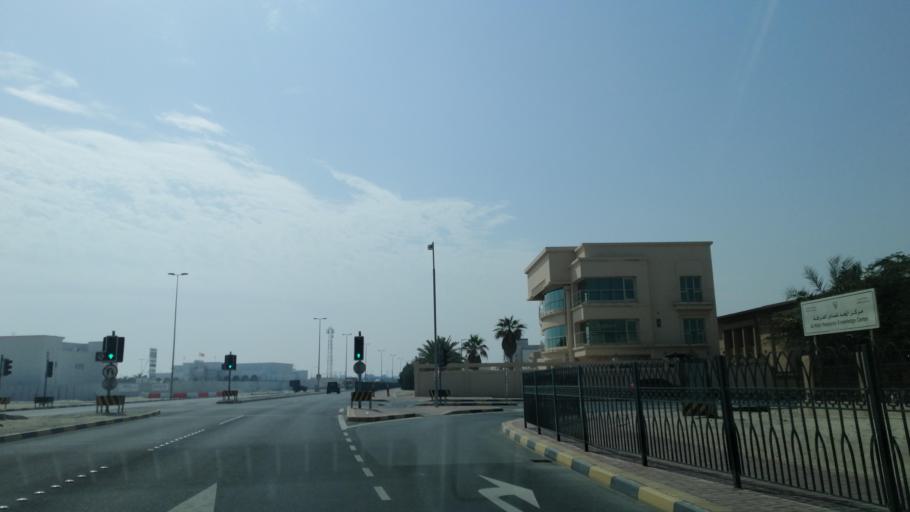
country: BH
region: Muharraq
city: Al Hadd
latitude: 26.2505
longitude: 50.6572
